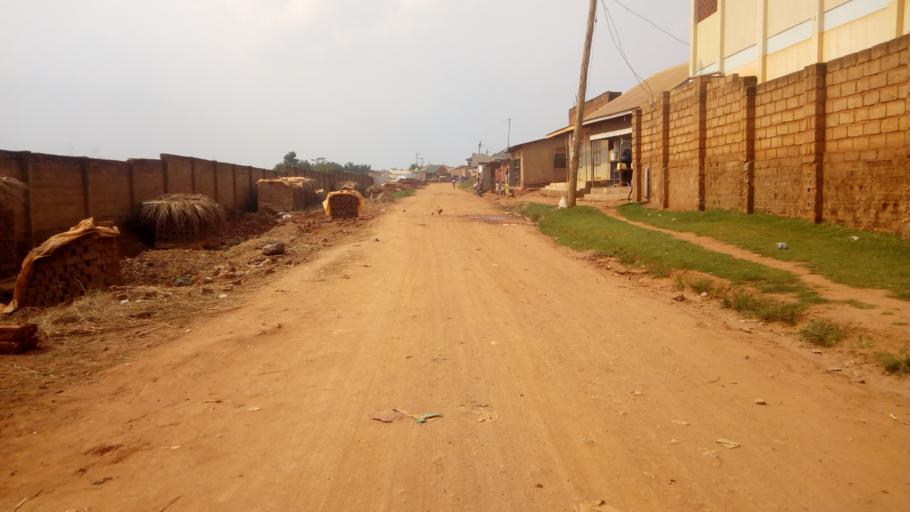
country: UG
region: Central Region
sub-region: Wakiso District
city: Kireka
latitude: 0.3219
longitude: 32.6527
